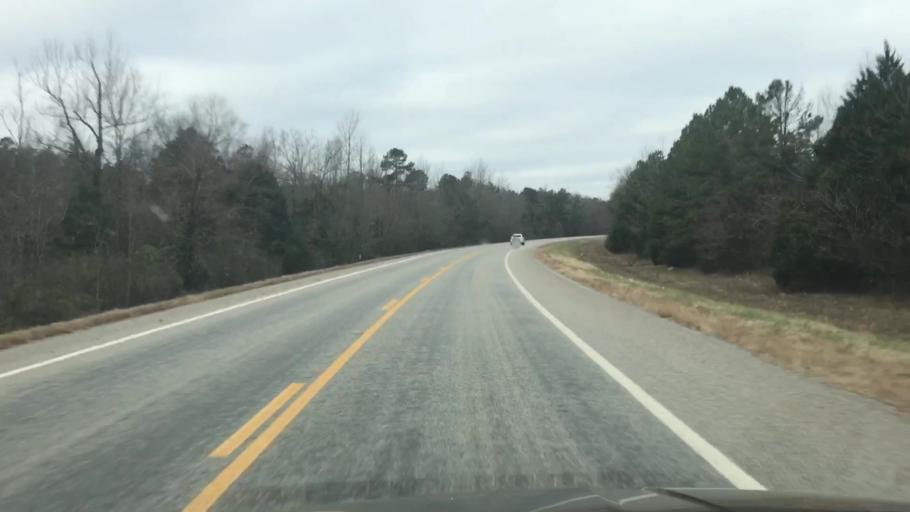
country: US
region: Arkansas
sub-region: Scott County
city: Waldron
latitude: 34.7040
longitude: -93.9257
